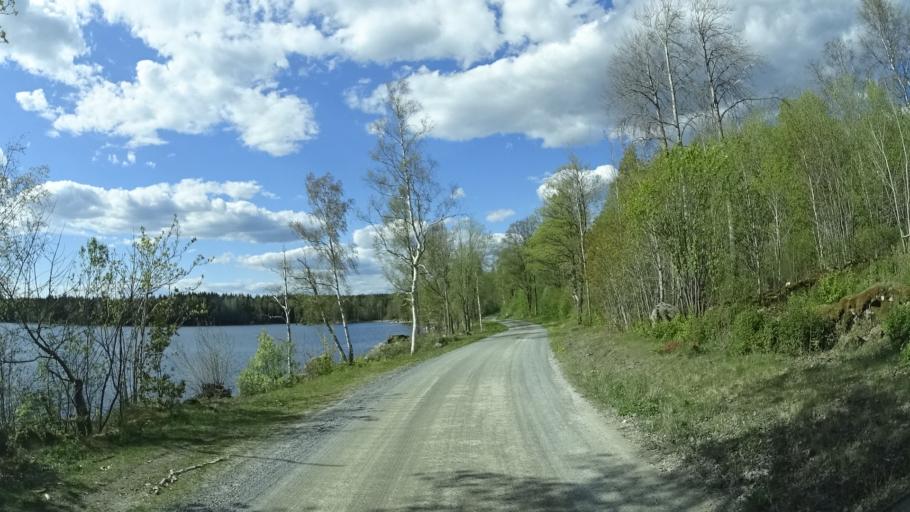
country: SE
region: OErebro
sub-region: Nora Kommun
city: As
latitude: 59.4463
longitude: 14.8108
